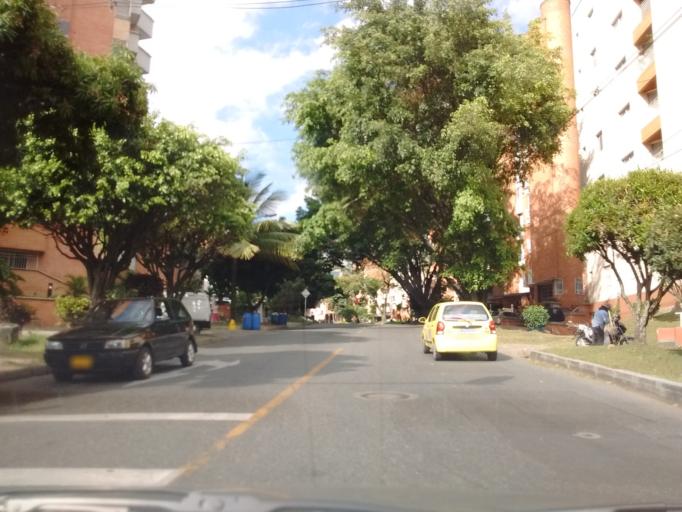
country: CO
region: Antioquia
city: Medellin
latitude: 6.2441
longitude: -75.6069
